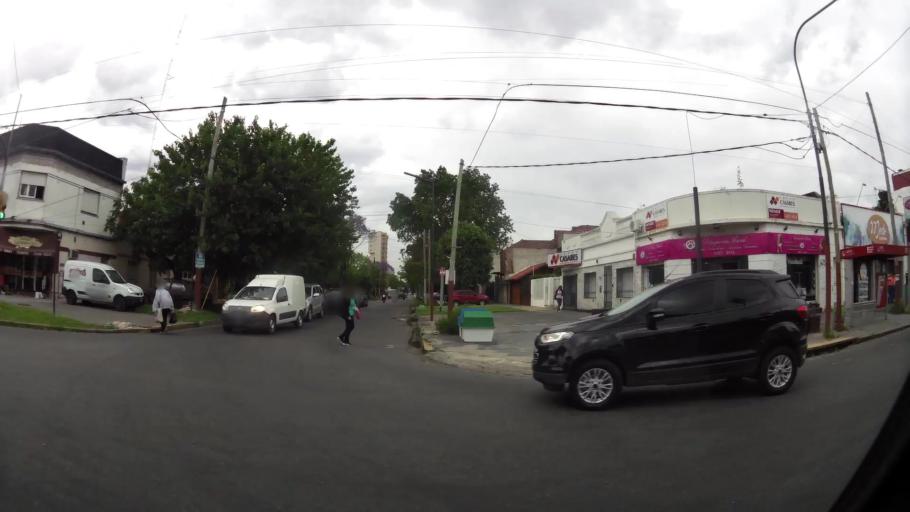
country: AR
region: Buenos Aires
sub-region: Partido de Lanus
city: Lanus
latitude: -34.6959
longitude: -58.3949
